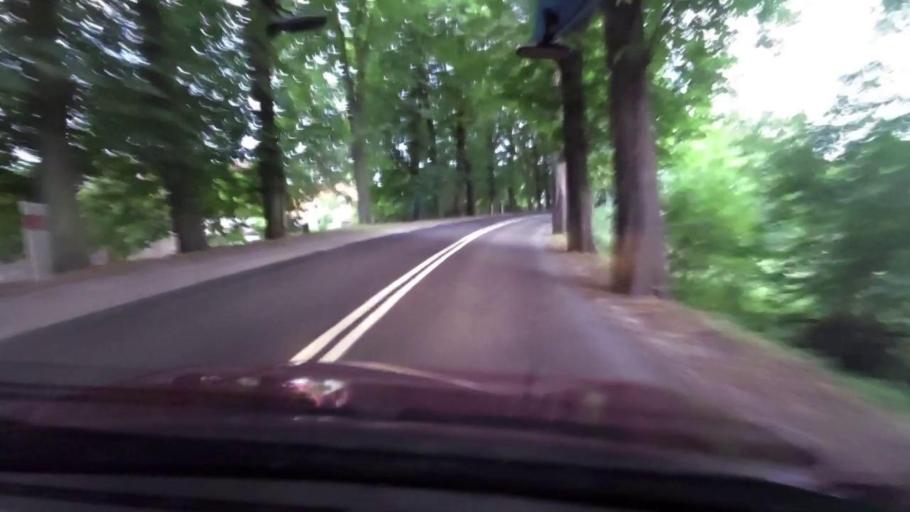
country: PL
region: West Pomeranian Voivodeship
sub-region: Powiat koszalinski
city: Sianow
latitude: 54.1863
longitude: 16.2446
